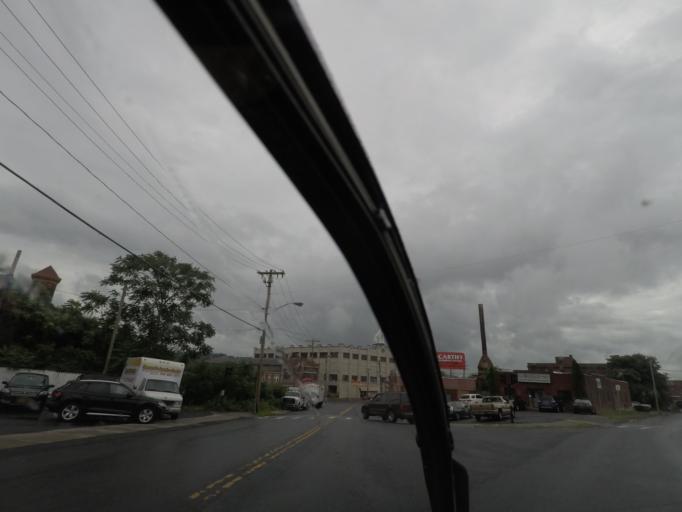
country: US
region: New York
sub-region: Albany County
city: Albany
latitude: 42.6655
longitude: -73.7433
